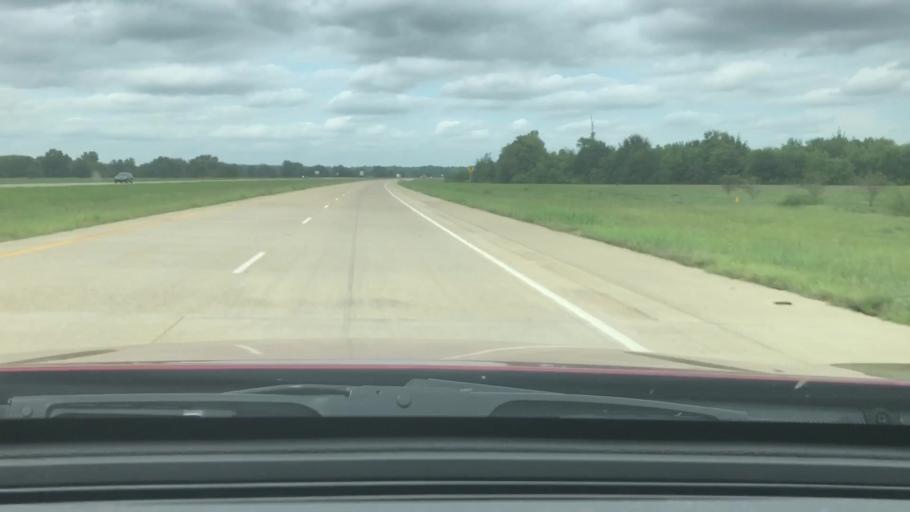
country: US
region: Louisiana
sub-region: Caddo Parish
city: Oil City
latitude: 32.7696
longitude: -93.8890
